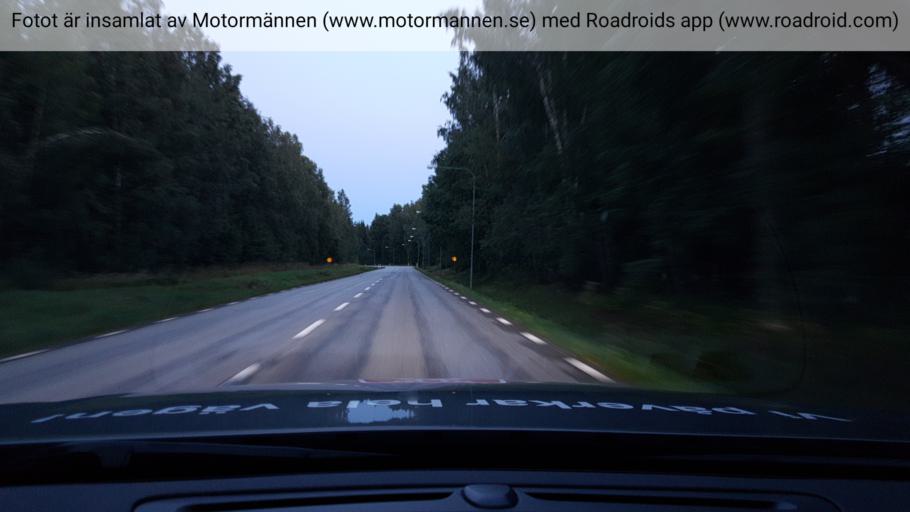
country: SE
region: OErebro
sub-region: Ljusnarsbergs Kommun
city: Kopparberg
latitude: 59.8695
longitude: 15.0185
